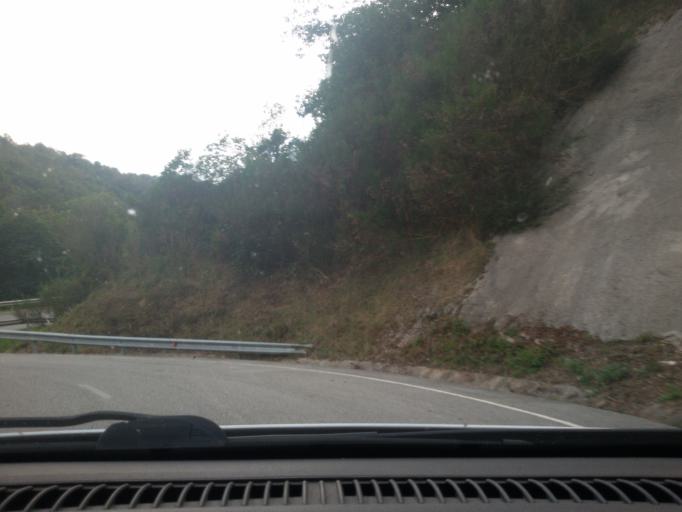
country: ES
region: Asturias
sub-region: Province of Asturias
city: Bimenes
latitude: 43.3384
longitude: -5.5774
